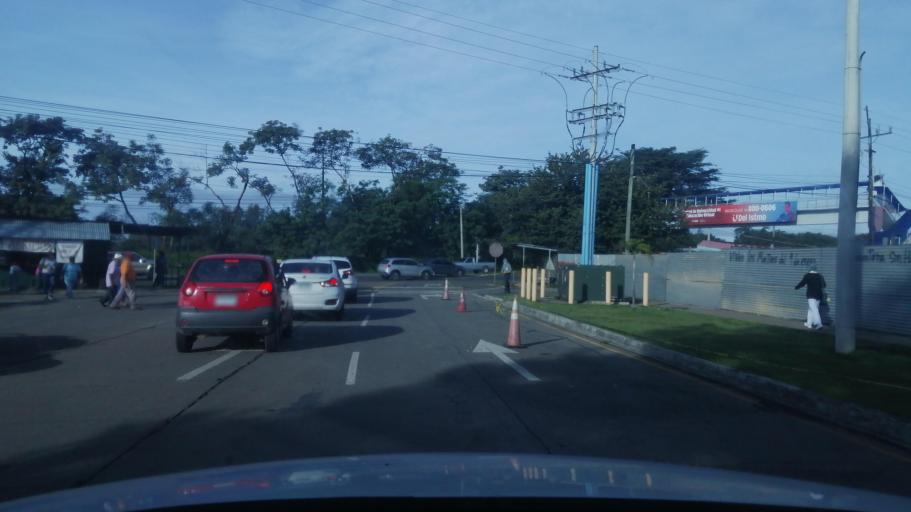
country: PA
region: Chiriqui
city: David
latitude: 8.4303
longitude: -82.4544
